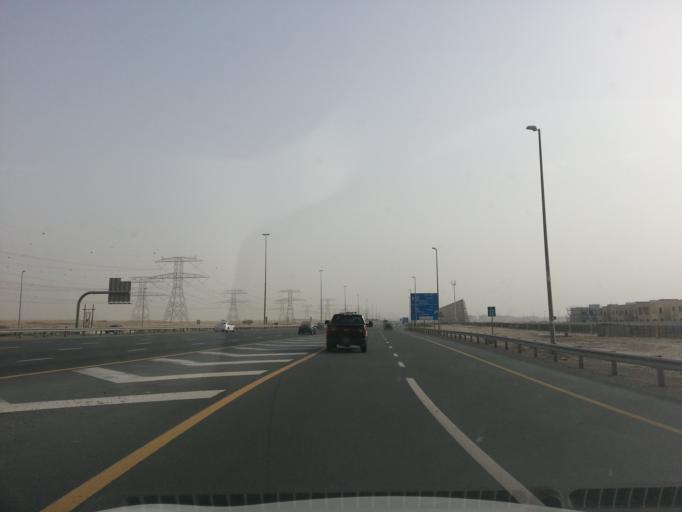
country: AE
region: Dubai
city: Dubai
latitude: 25.0202
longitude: 55.2785
